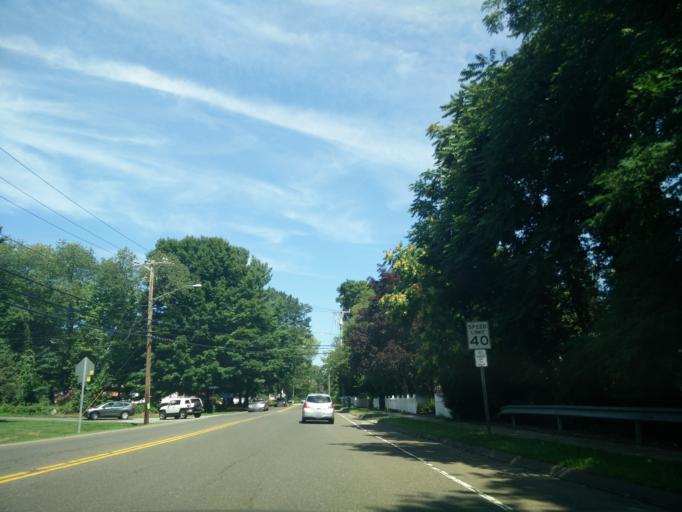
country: US
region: Connecticut
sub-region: Middlesex County
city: Clinton
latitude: 41.2941
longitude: -72.5313
